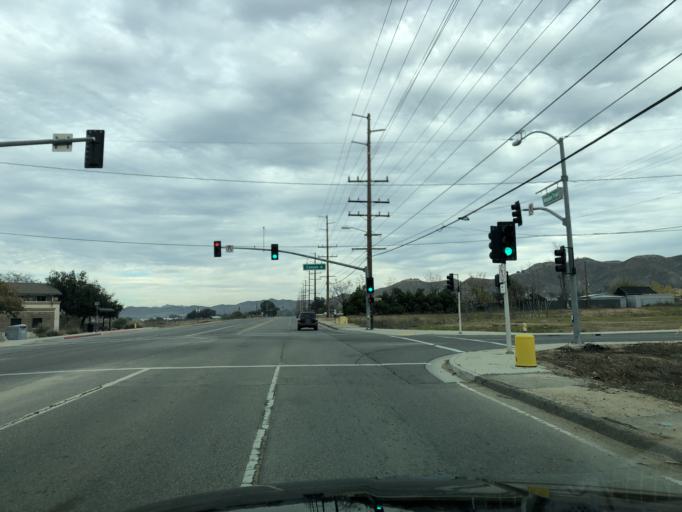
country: US
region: California
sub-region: Riverside County
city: Sedco Hills
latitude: 33.6230
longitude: -117.2901
